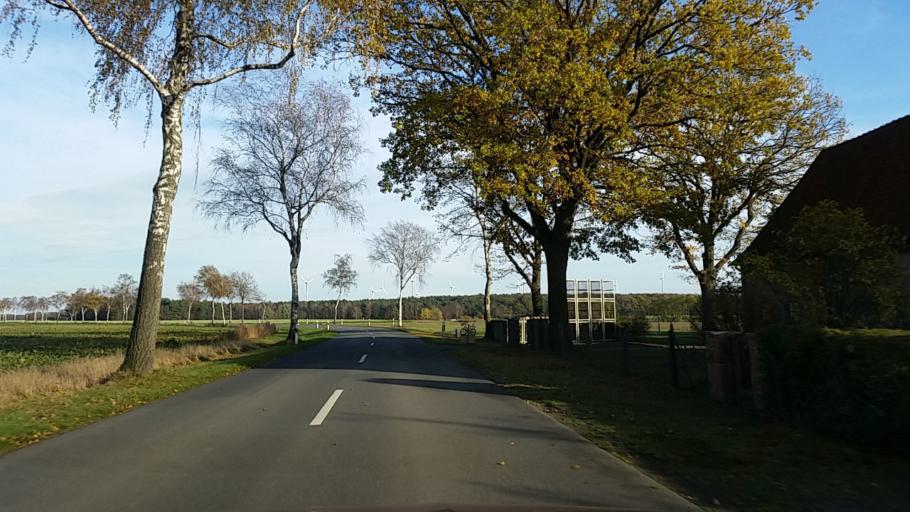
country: DE
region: Lower Saxony
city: Gross Oesingen
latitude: 52.6587
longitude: 10.4961
